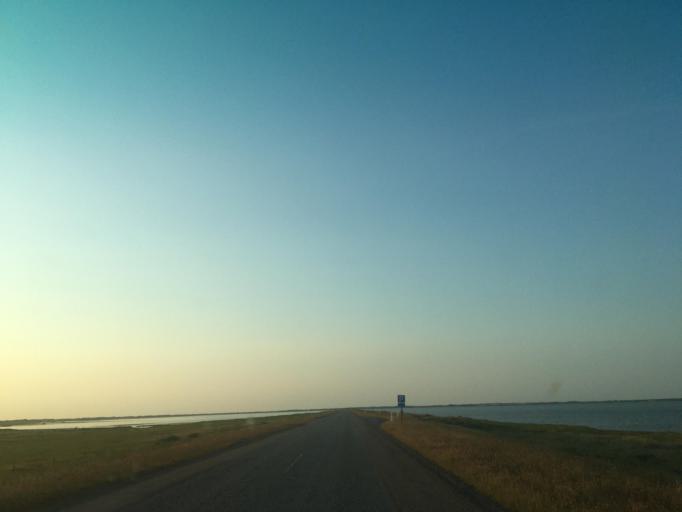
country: DK
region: Central Jutland
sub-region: Lemvig Kommune
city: Thyboron
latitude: 56.7309
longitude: 8.2498
